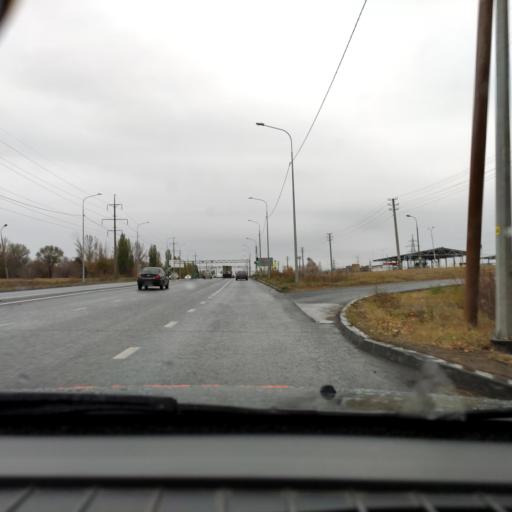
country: RU
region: Samara
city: Tol'yatti
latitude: 53.5661
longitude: 49.2907
